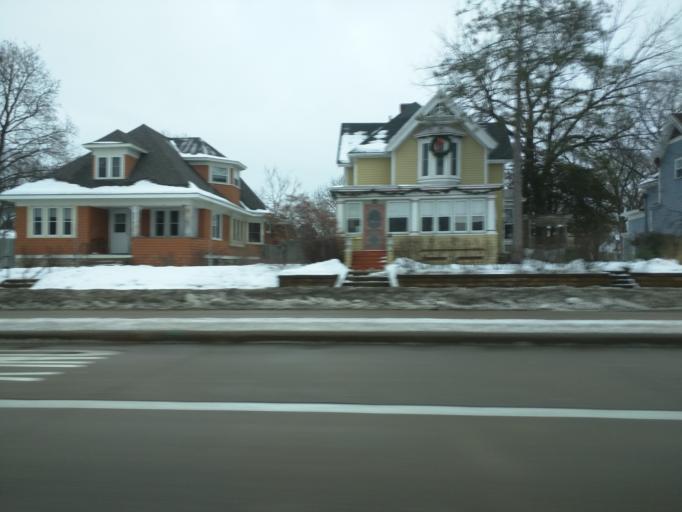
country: US
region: Wisconsin
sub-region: La Crosse County
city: La Crosse
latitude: 43.8030
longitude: -91.2396
